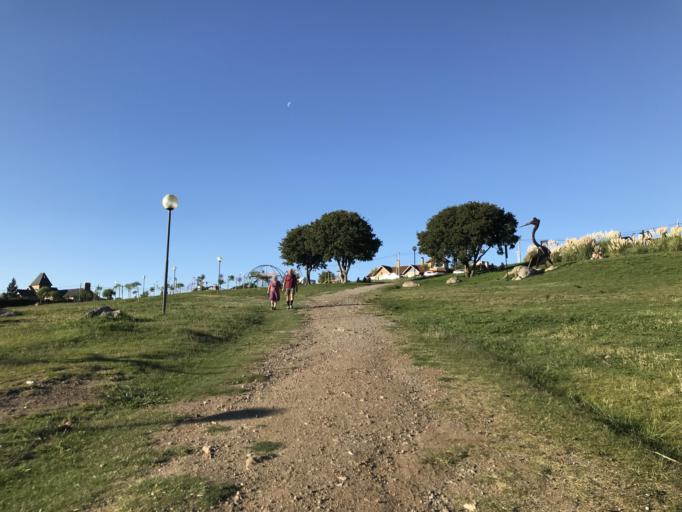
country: AR
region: Buenos Aires
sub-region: Partido de Tandil
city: Tandil
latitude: -37.3368
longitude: -59.1138
